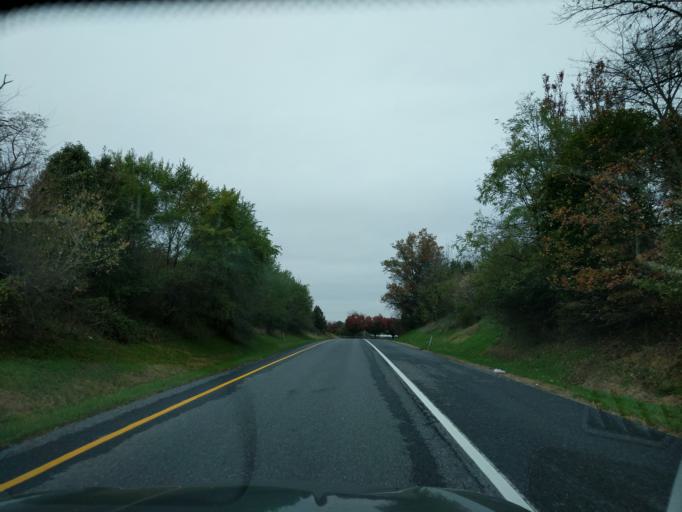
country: US
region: Maryland
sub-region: Washington County
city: Robinwood
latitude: 39.6013
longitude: -77.6803
